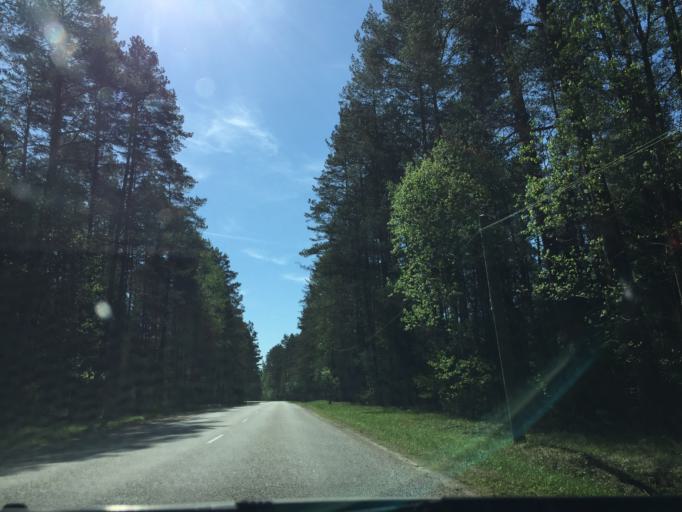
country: LV
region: Garkalne
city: Garkalne
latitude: 57.0181
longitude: 24.4408
